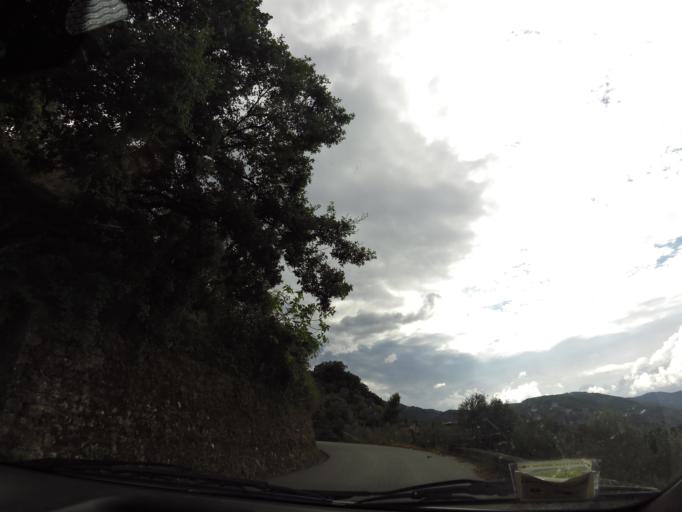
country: IT
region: Calabria
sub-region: Provincia di Reggio Calabria
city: Bivongi
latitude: 38.4802
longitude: 16.4555
